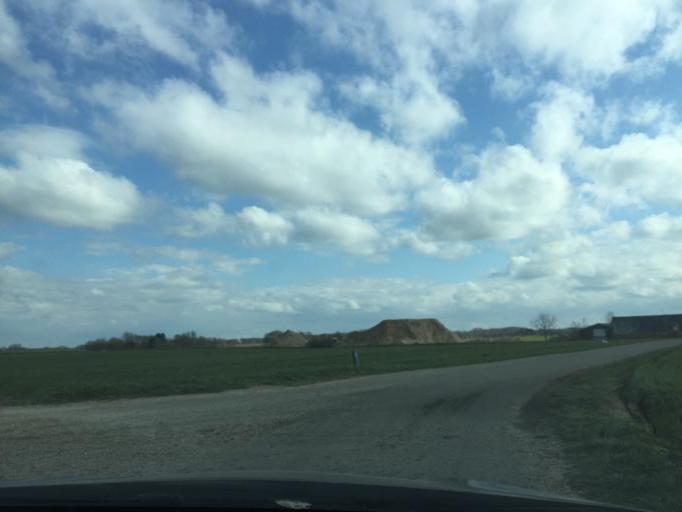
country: DK
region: South Denmark
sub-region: Faaborg-Midtfyn Kommune
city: Arslev
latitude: 55.3207
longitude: 10.4646
